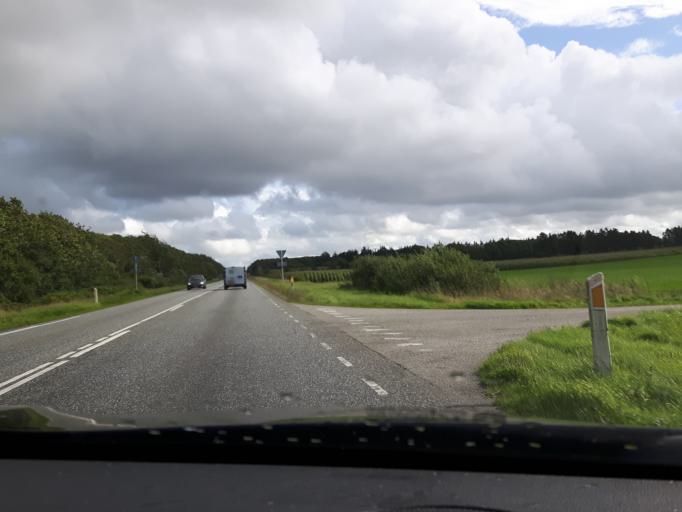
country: DK
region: Central Jutland
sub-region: Herning Kommune
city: Avlum
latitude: 56.2909
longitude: 8.7335
